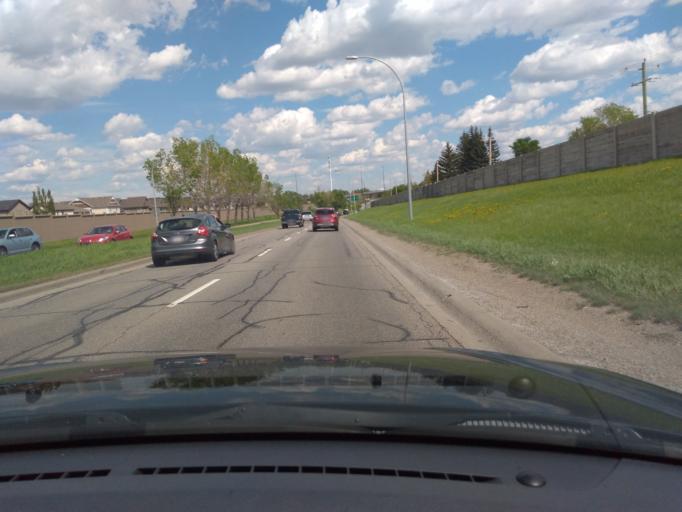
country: CA
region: Alberta
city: Calgary
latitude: 51.0010
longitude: -114.1256
